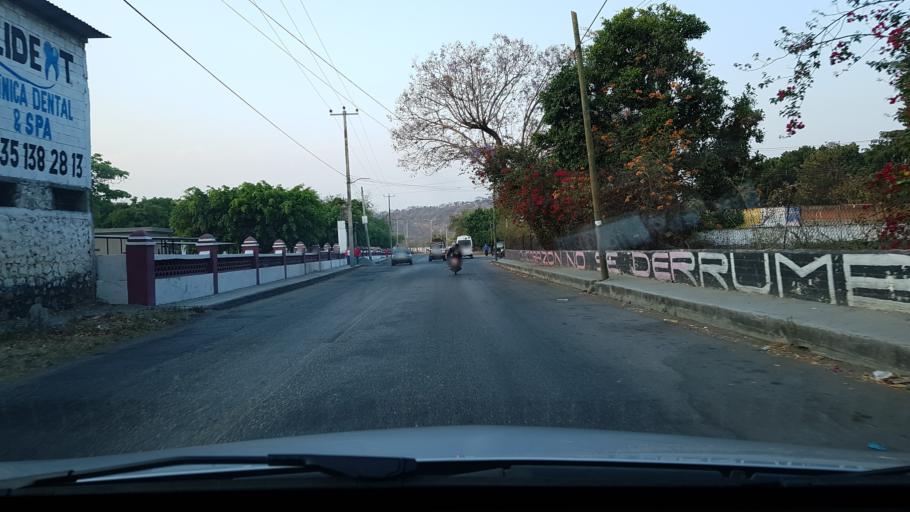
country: MX
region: Morelos
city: Jonacatepec de Leandro Valle
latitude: 18.6753
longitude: -98.8046
